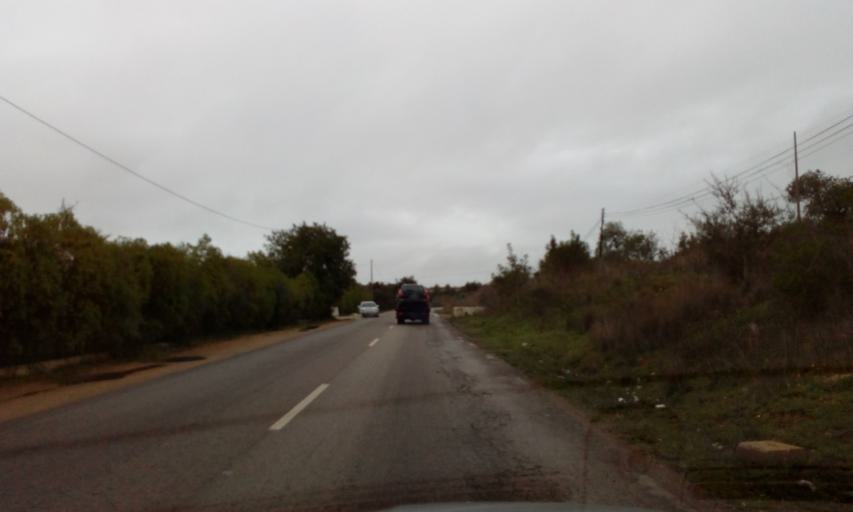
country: PT
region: Faro
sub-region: Albufeira
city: Ferreiras
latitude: 37.1371
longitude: -8.2655
